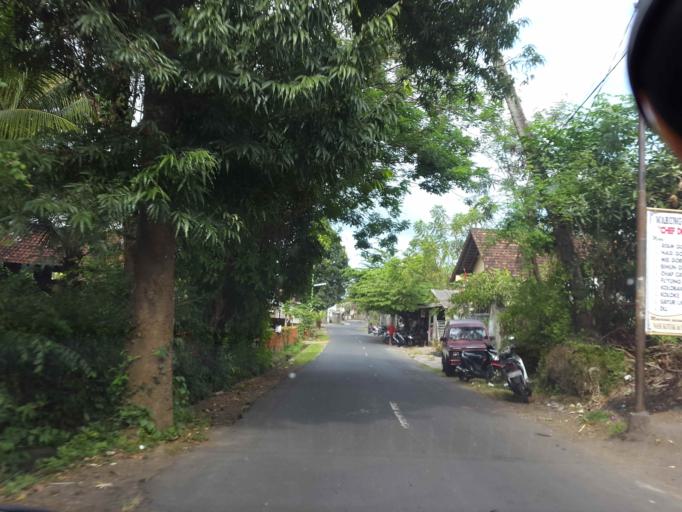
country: ID
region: Bali
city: Klungkung
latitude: -8.5325
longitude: 115.3862
